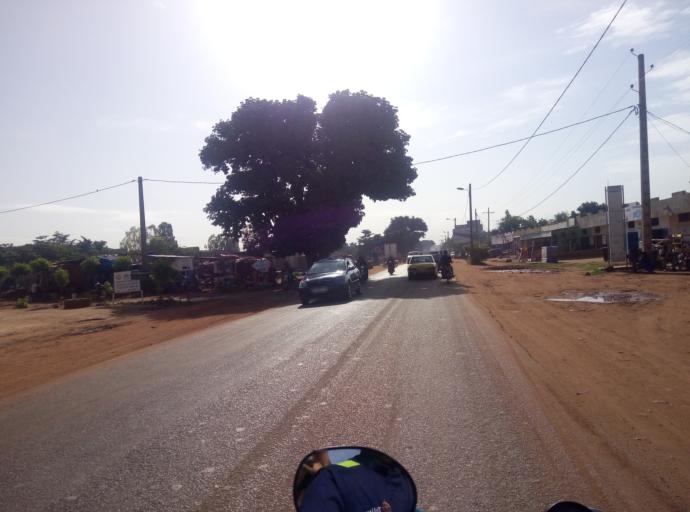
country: ML
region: Bamako
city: Bamako
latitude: 12.6521
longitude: -7.9469
